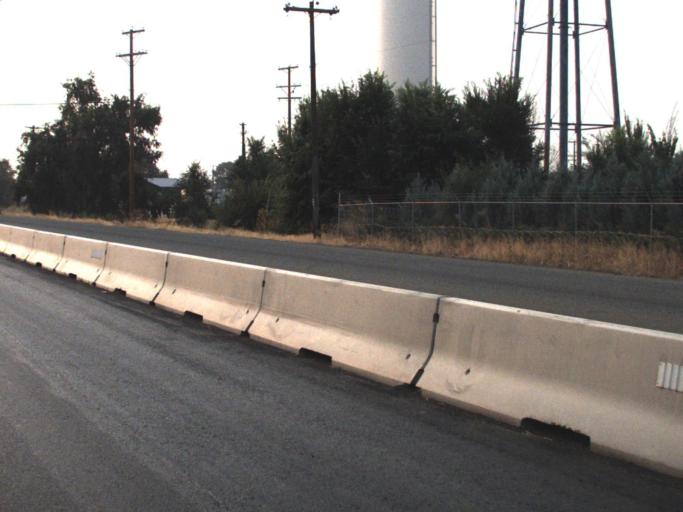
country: US
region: Washington
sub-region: Yakima County
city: Toppenish
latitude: 46.3784
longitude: -120.3363
